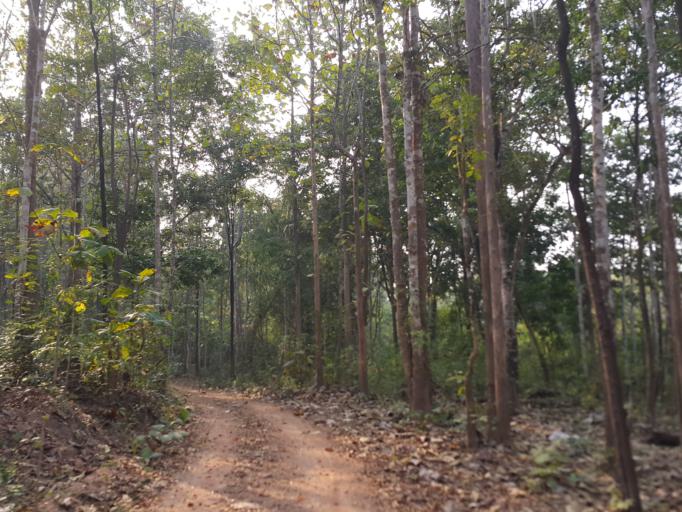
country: TH
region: Lamphun
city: Li
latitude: 17.6069
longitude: 98.9465
